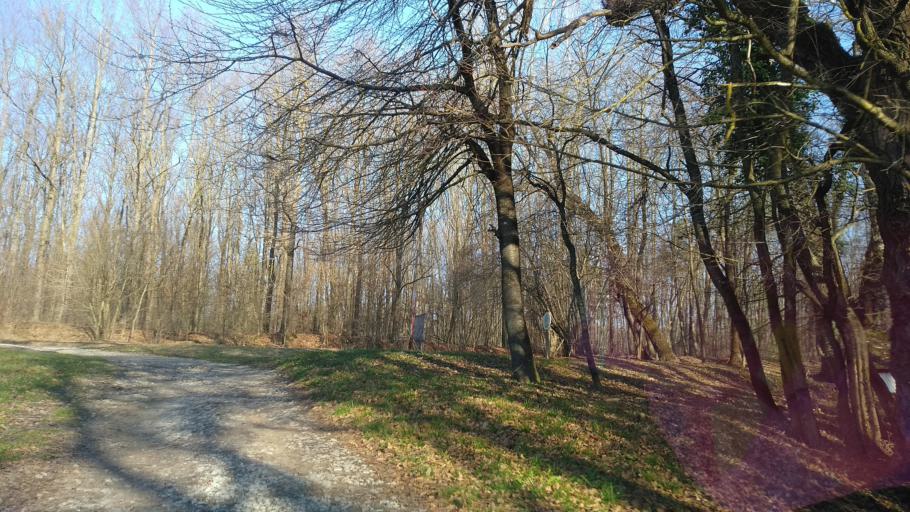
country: HU
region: Somogy
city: Barcs
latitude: 45.9517
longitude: 17.5129
